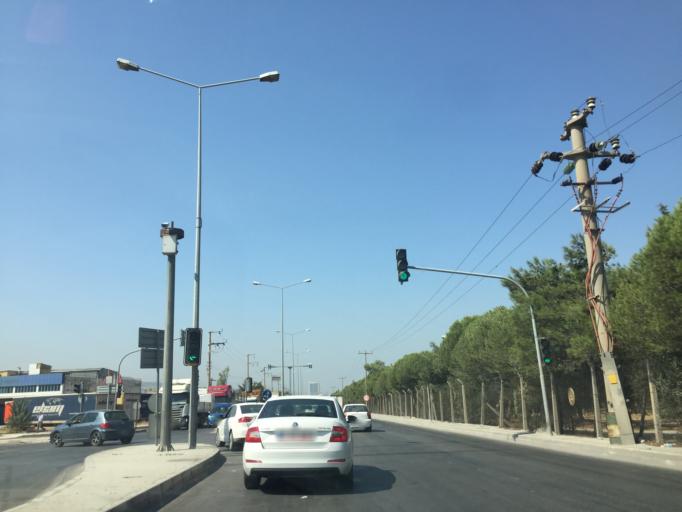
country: TR
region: Izmir
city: Bornova
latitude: 38.4412
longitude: 27.2697
